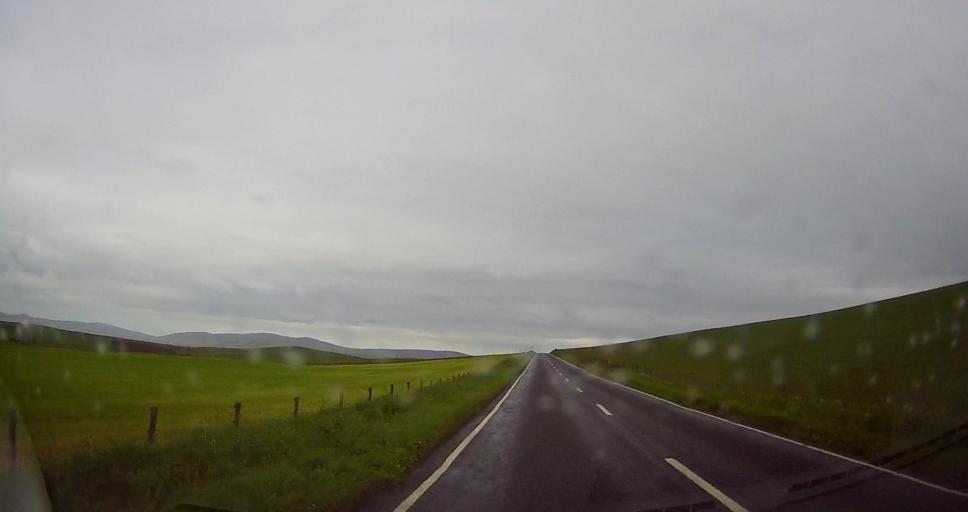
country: GB
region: Scotland
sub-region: Orkney Islands
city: Stromness
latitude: 59.0046
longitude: -3.2886
